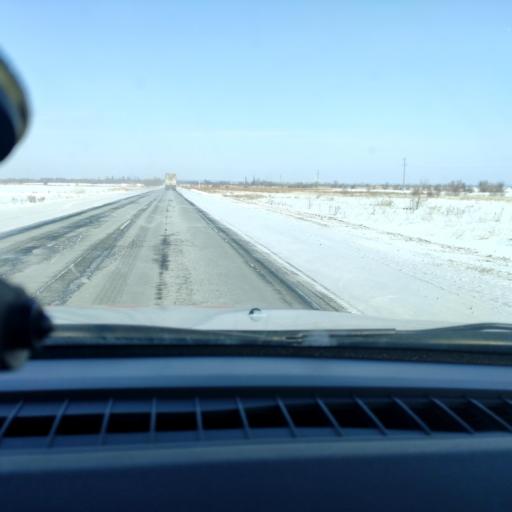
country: RU
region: Samara
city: Smyshlyayevka
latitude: 53.1603
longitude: 50.4569
